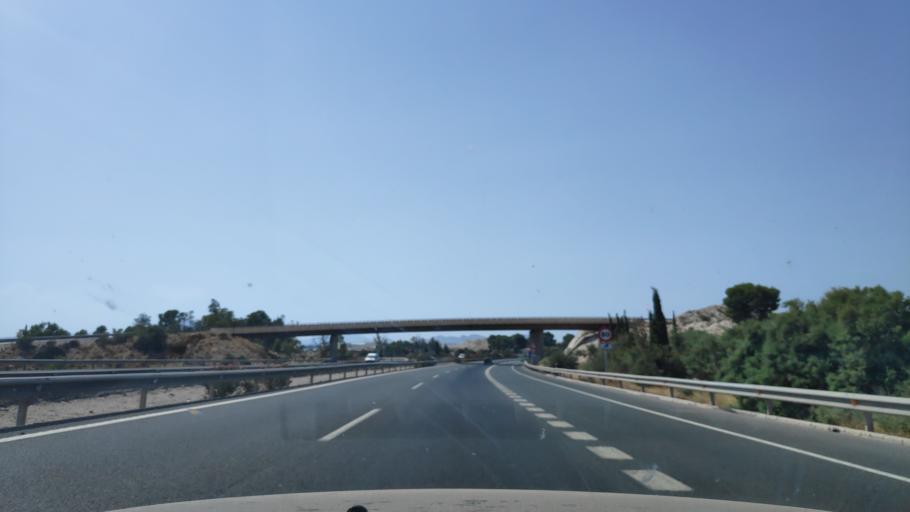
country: ES
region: Murcia
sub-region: Murcia
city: Molina de Segura
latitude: 38.0817
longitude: -1.2187
